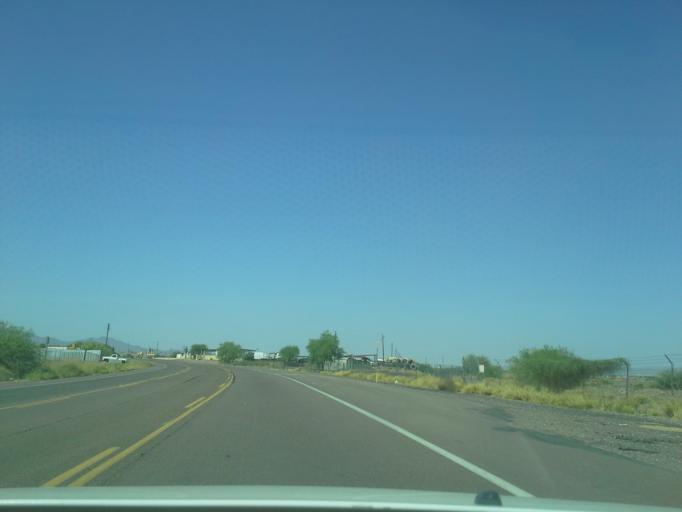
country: US
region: Arizona
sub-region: Maricopa County
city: Laveen
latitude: 33.4066
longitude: -112.1421
